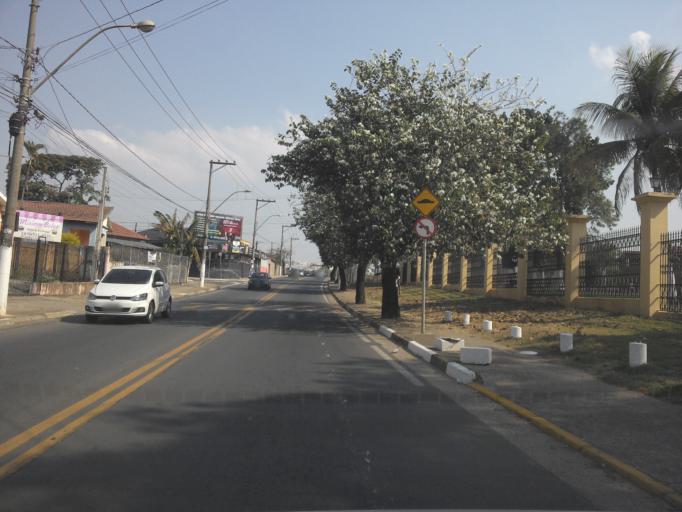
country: BR
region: Sao Paulo
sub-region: Hortolandia
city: Hortolandia
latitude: -22.8640
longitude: -47.2239
